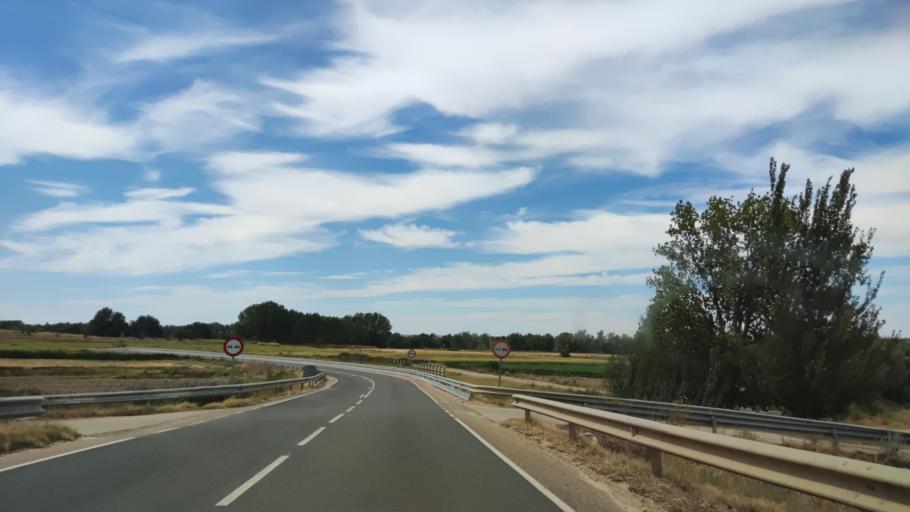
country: ES
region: Castille and Leon
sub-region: Provincia de Zamora
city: Villalazan
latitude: 41.4953
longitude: -5.5932
